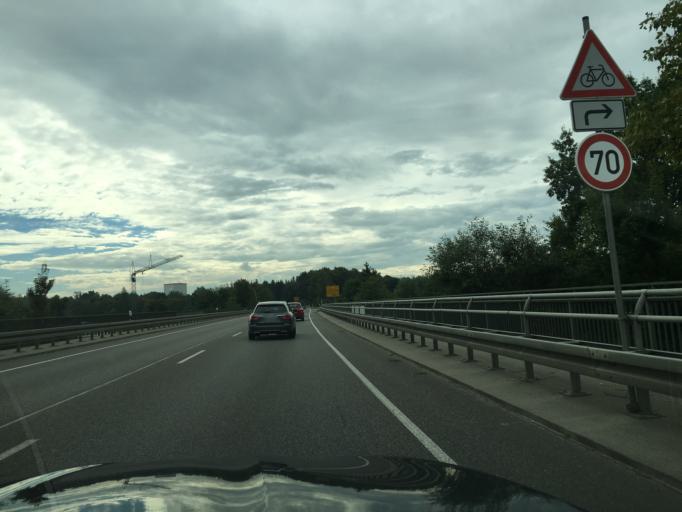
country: DE
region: Baden-Wuerttemberg
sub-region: Tuebingen Region
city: Riedlingen
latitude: 48.1549
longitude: 9.4887
